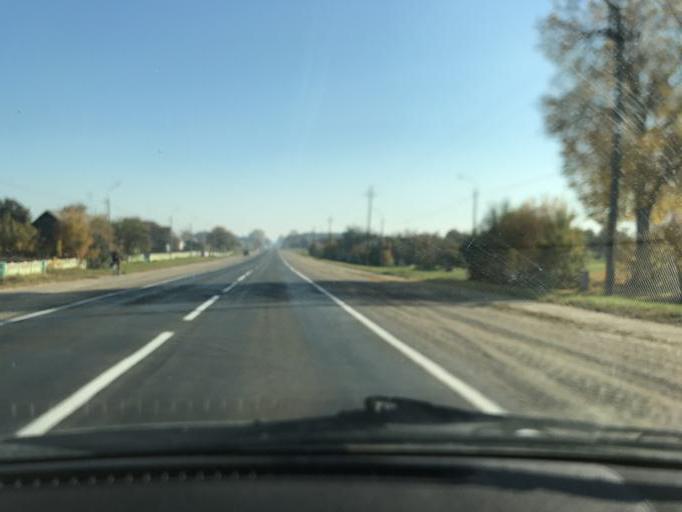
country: BY
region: Minsk
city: Klyetsk
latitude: 52.9628
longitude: 26.4611
